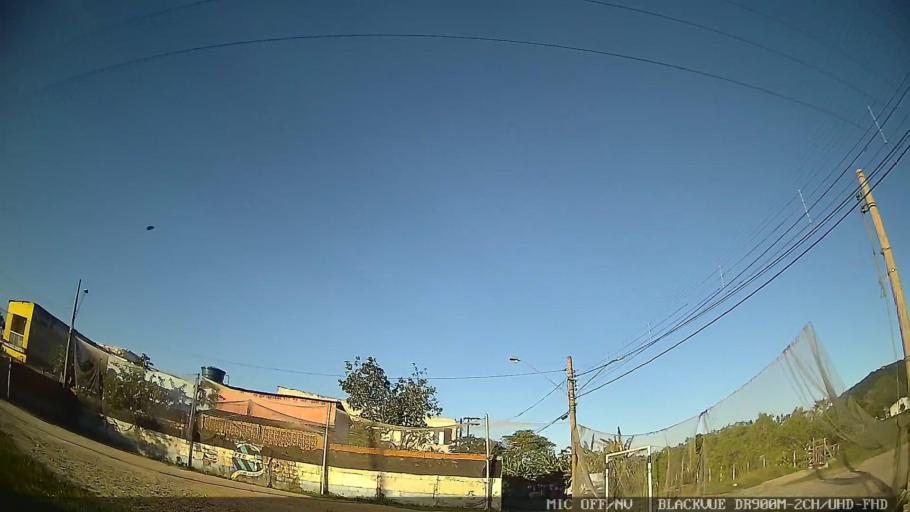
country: BR
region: Sao Paulo
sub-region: Guaruja
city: Guaruja
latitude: -23.9675
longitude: -46.2758
